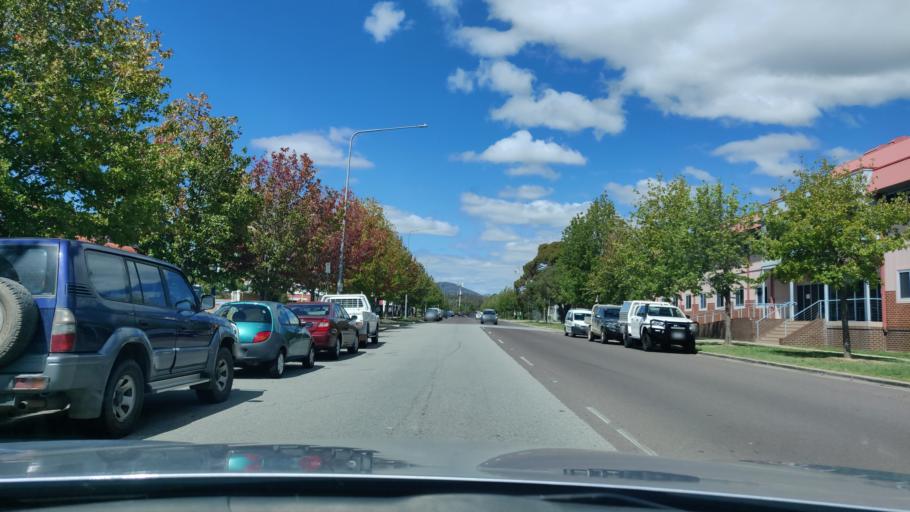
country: AU
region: Australian Capital Territory
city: Macarthur
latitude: -35.4205
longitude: 149.0682
